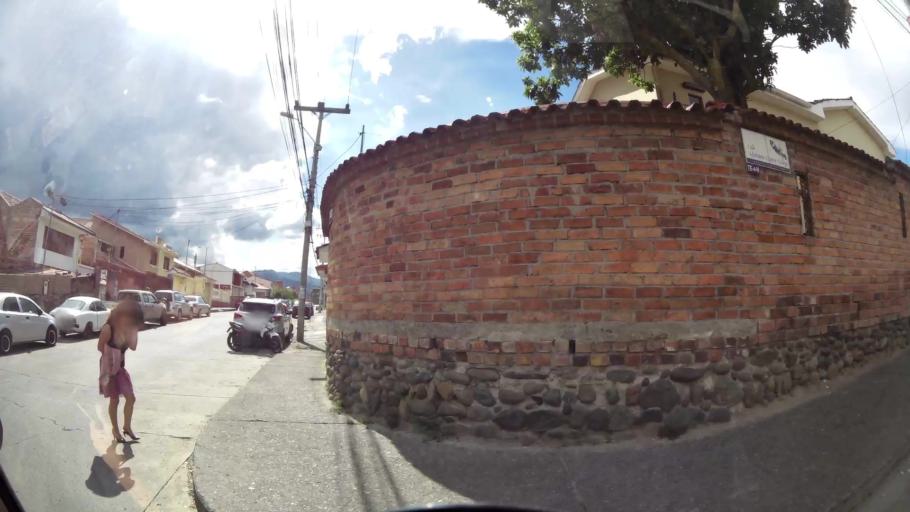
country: EC
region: Azuay
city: Cuenca
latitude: -2.8876
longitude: -78.9993
